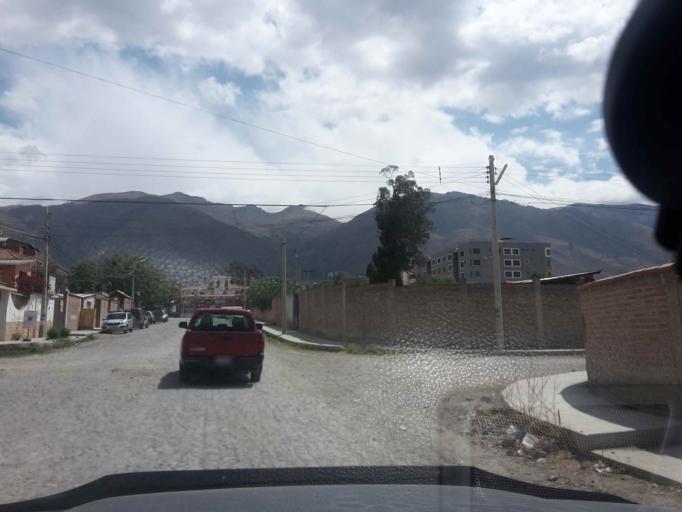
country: BO
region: Cochabamba
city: Cochabamba
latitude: -17.3485
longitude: -66.1991
